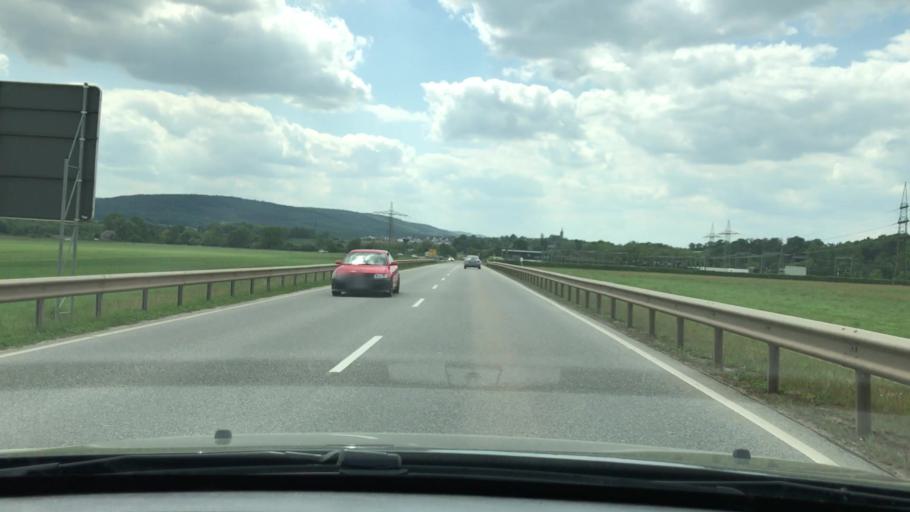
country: DE
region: Rheinland-Pfalz
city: Altrich
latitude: 49.9737
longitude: 6.9234
